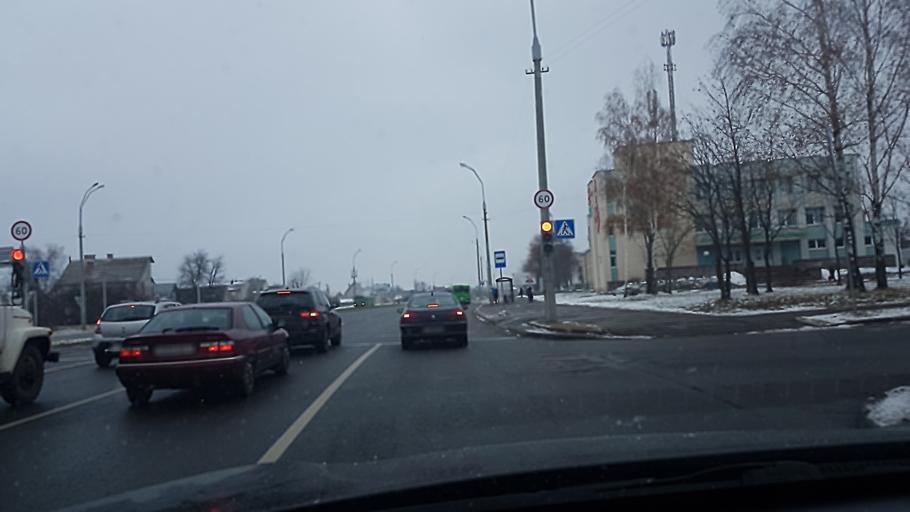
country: BY
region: Minsk
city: Bal'shavik
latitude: 53.9526
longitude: 27.5351
